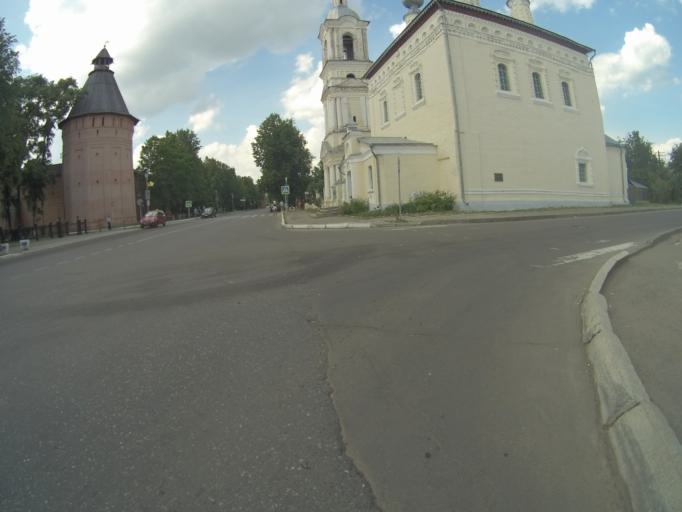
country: RU
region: Vladimir
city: Suzdal'
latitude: 56.4318
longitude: 40.4435
